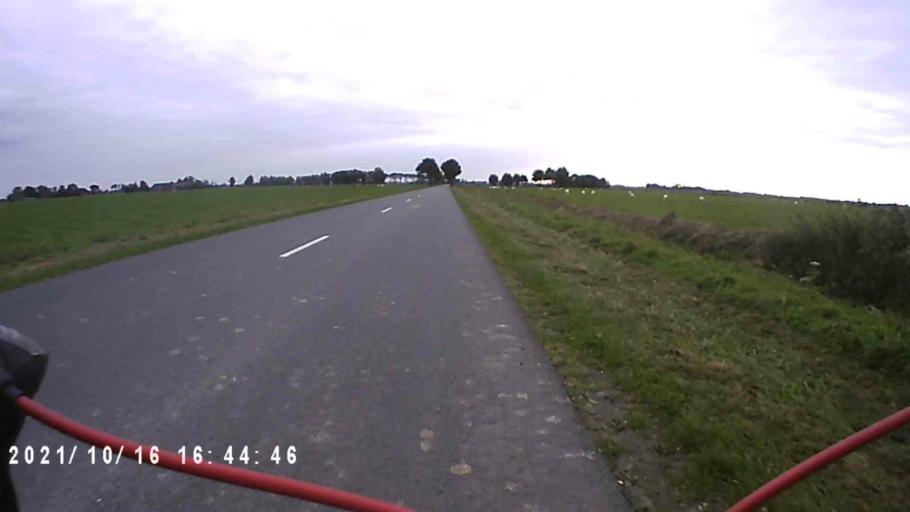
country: NL
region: Friesland
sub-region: Gemeente Dongeradeel
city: Anjum
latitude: 53.3669
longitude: 6.1420
